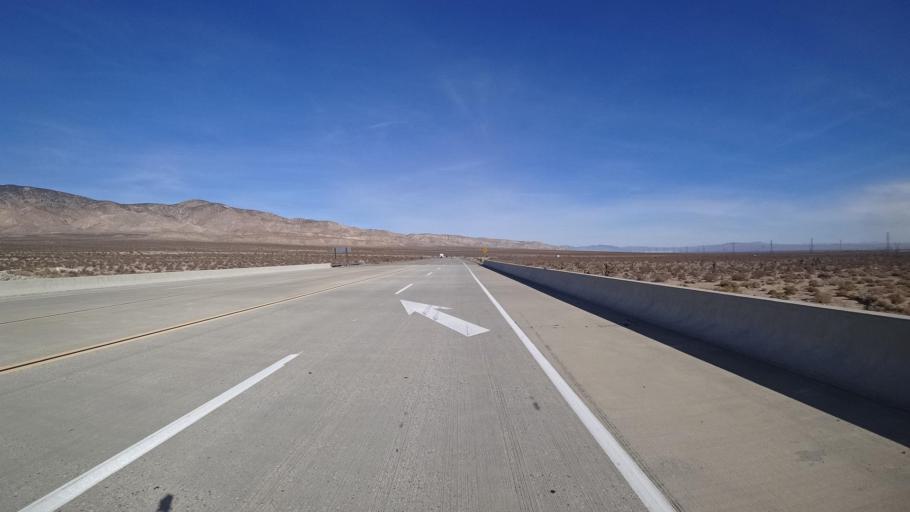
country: US
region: California
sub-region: Kern County
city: Mojave
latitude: 35.1182
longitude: -118.1773
